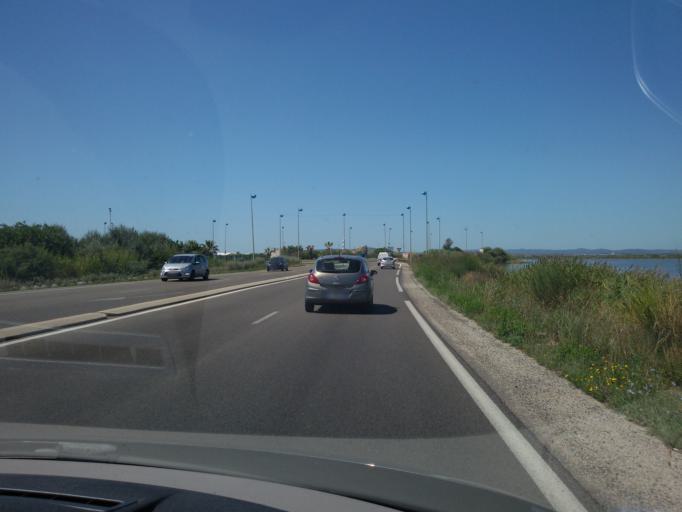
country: FR
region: Languedoc-Roussillon
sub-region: Departement de l'Herault
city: Palavas-les-Flots
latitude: 43.5347
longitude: 3.9405
